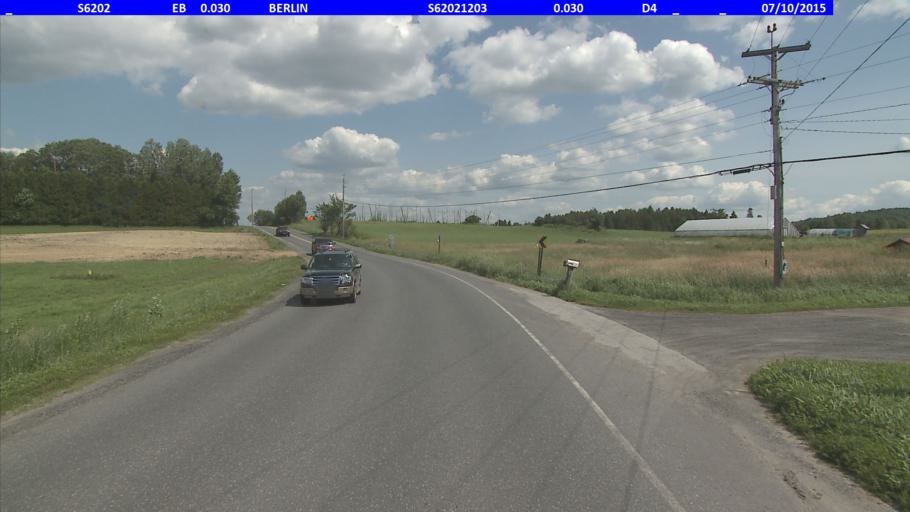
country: US
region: Vermont
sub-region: Washington County
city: South Barre
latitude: 44.1927
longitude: -72.5552
